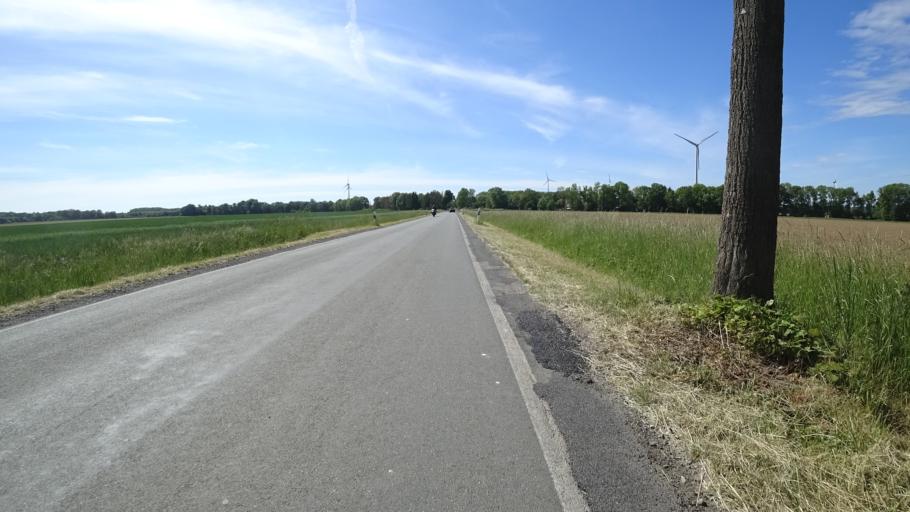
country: DE
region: North Rhine-Westphalia
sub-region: Regierungsbezirk Detmold
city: Rheda-Wiedenbruck
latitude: 51.8226
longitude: 8.2473
